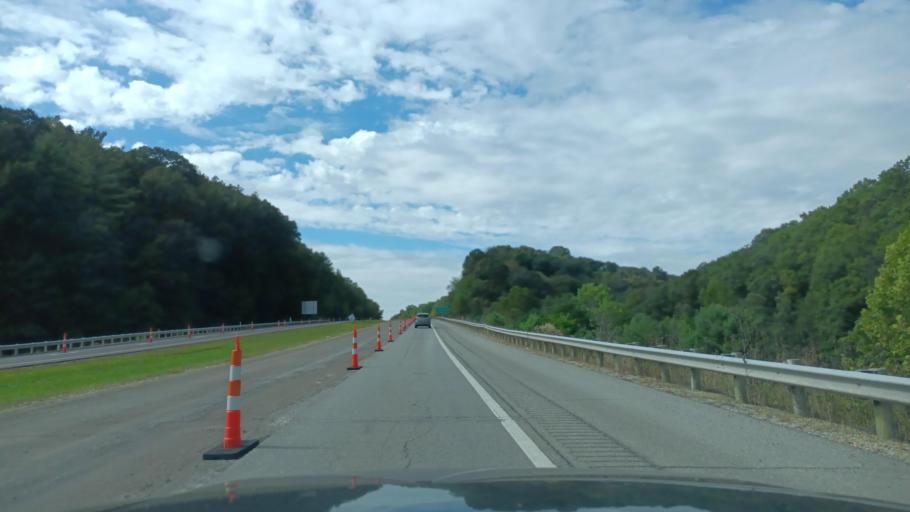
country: US
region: West Virginia
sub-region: Ritchie County
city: Harrisville
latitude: 39.2606
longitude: -81.0841
